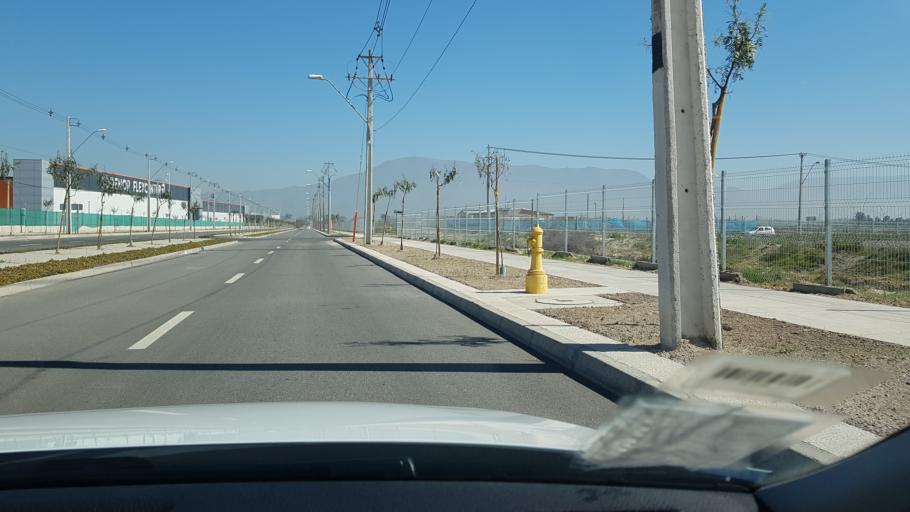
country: CL
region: Santiago Metropolitan
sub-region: Provincia de Santiago
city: Lo Prado
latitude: -33.4258
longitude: -70.7883
